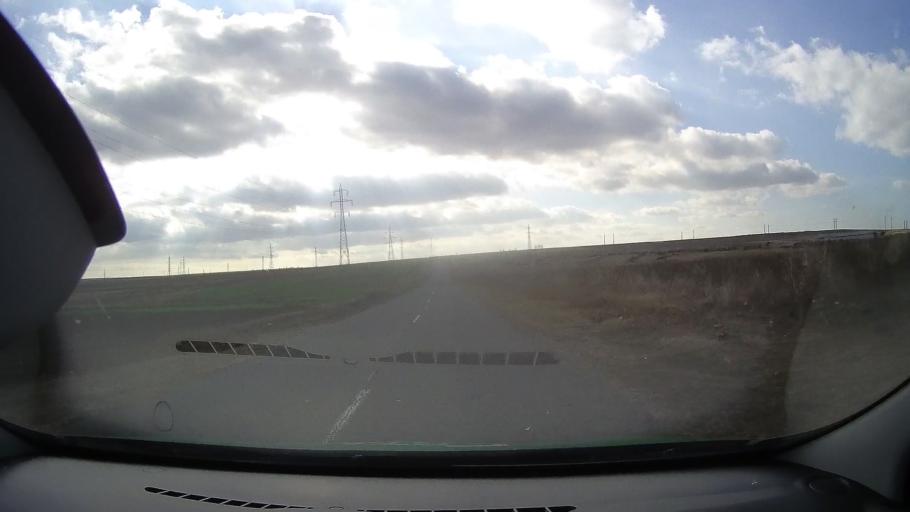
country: RO
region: Constanta
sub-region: Comuna Sacele
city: Sacele
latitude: 44.4980
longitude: 28.6591
